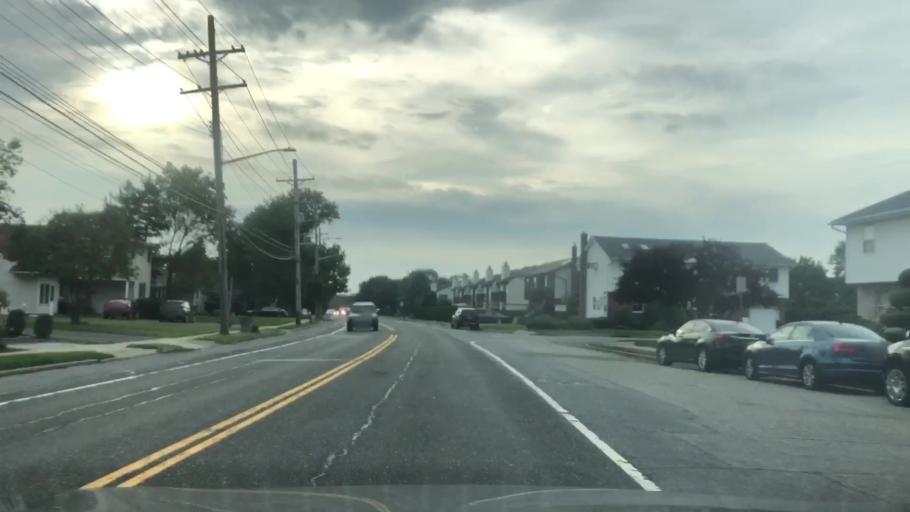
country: US
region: New York
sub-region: Nassau County
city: North Wantagh
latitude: 40.6939
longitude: -73.5021
